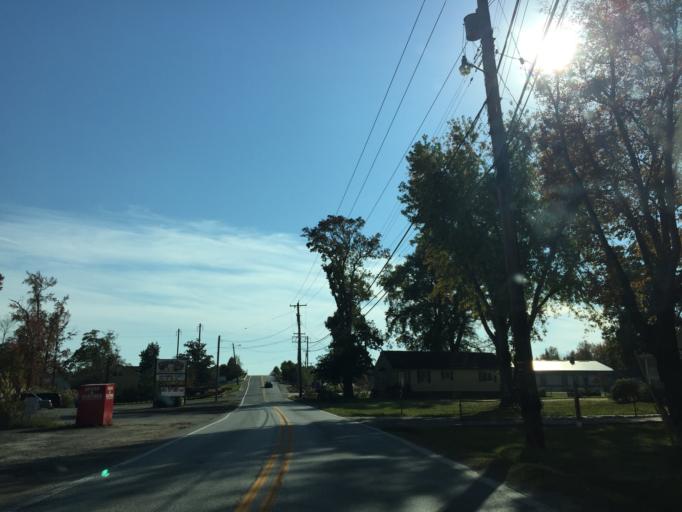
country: US
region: Maryland
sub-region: Baltimore County
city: Bowleys Quarters
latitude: 39.3485
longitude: -76.3941
